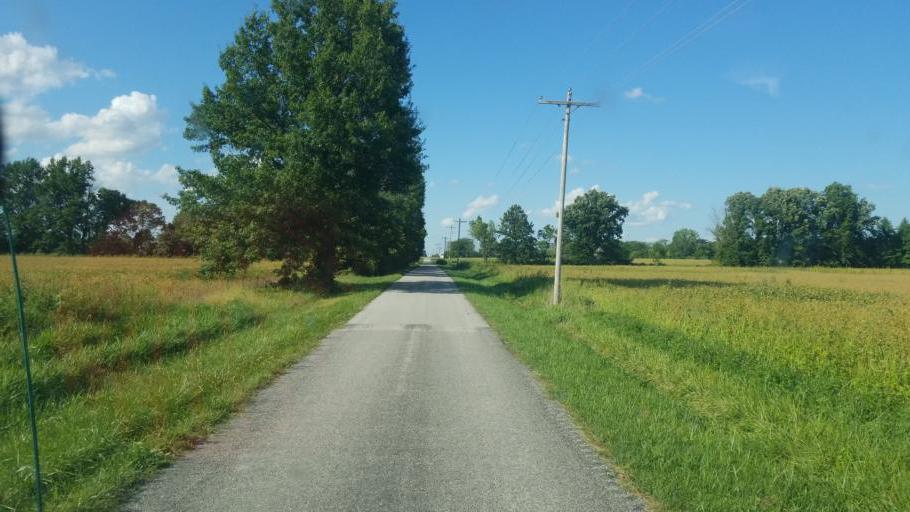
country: US
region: Ohio
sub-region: Marion County
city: Marion
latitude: 40.6279
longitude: -83.2694
